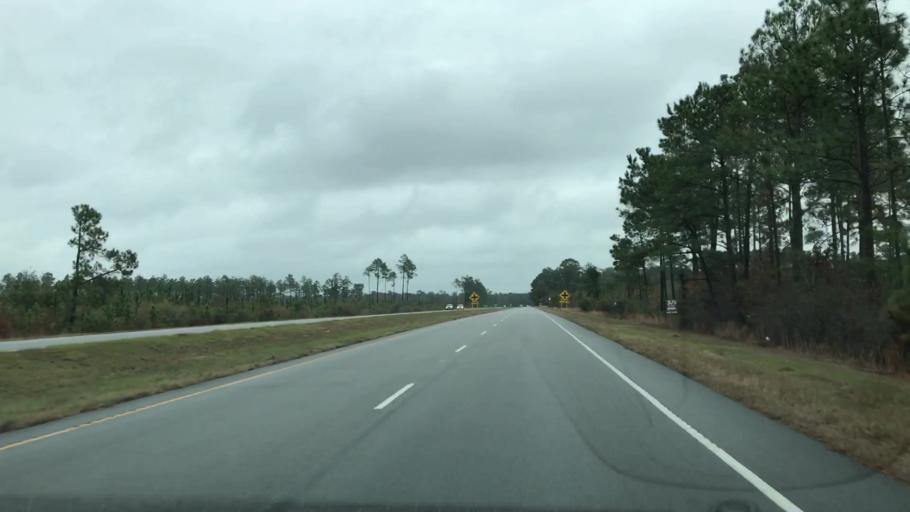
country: US
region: South Carolina
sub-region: Charleston County
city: Awendaw
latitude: 33.1697
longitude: -79.4199
